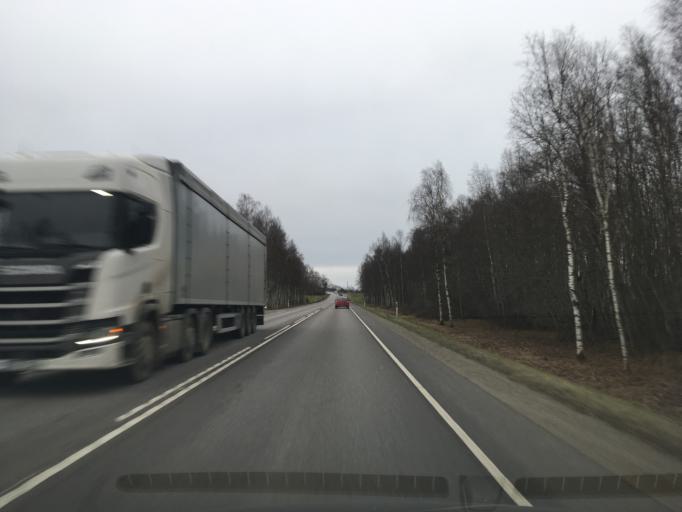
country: EE
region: Laeaene-Virumaa
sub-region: Someru vald
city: Someru
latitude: 59.3866
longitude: 26.3990
